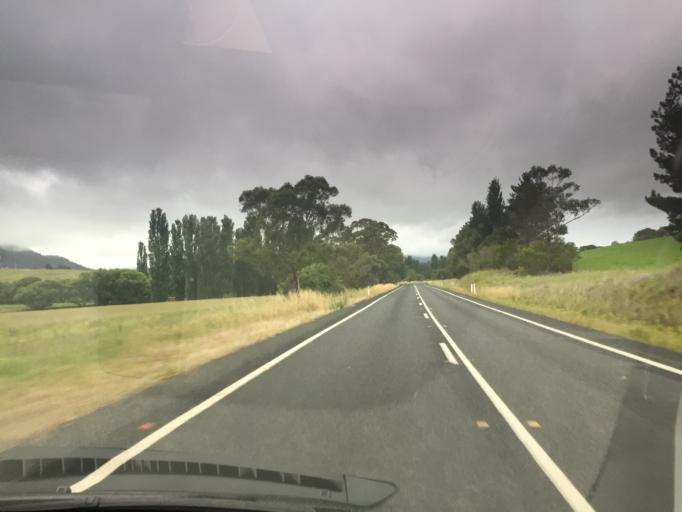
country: AU
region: New South Wales
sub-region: Bega Valley
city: Bega
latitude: -36.6124
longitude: 149.5257
